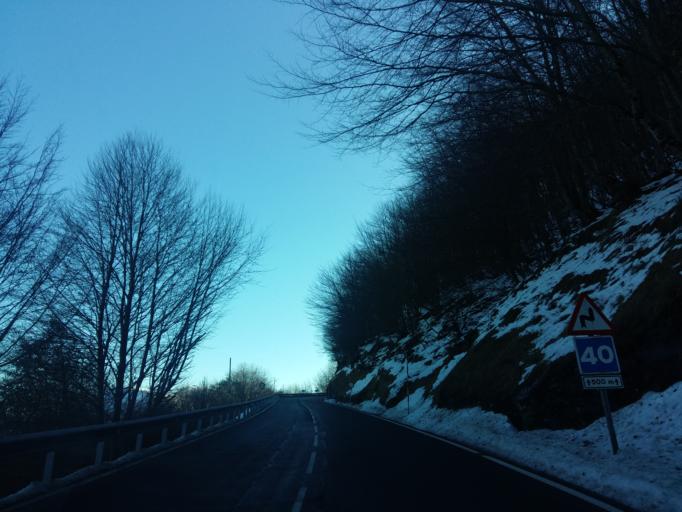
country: ES
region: Basque Country
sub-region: Bizkaia
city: Lanestosa
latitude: 43.1559
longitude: -3.4495
